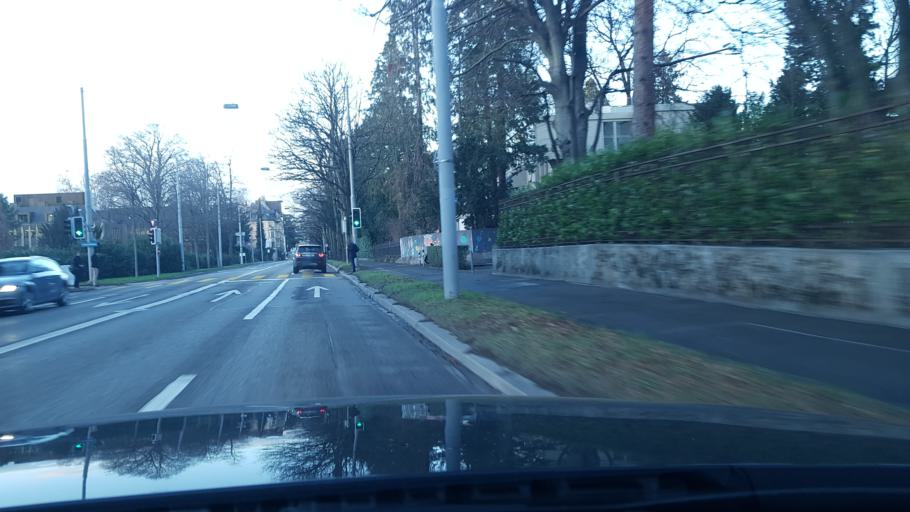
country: CH
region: Zurich
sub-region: Bezirk Zuerich
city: Zuerich (Kreis 8) / Seefeld
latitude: 47.3571
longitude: 8.5511
